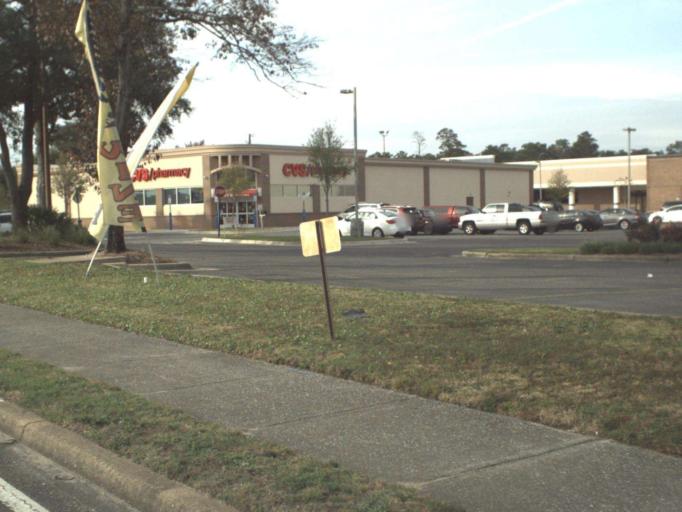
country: US
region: Florida
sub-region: Okaloosa County
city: Niceville
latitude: 30.5163
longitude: -86.4672
